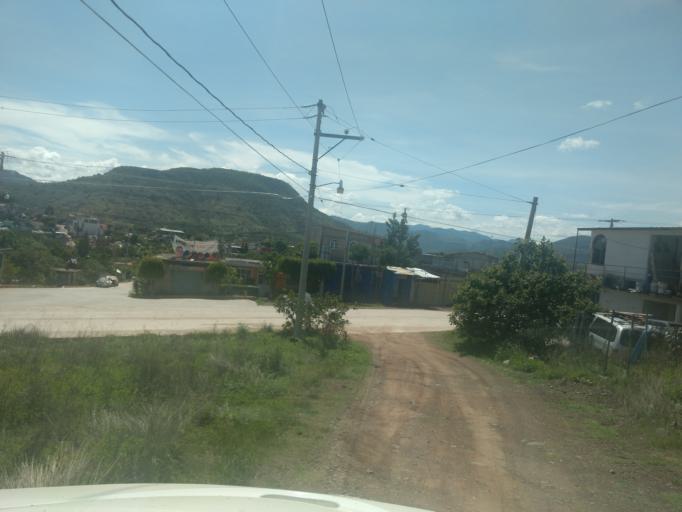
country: MX
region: Oaxaca
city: Ciudad de Huajuapam de Leon
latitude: 17.8246
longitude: -97.7844
